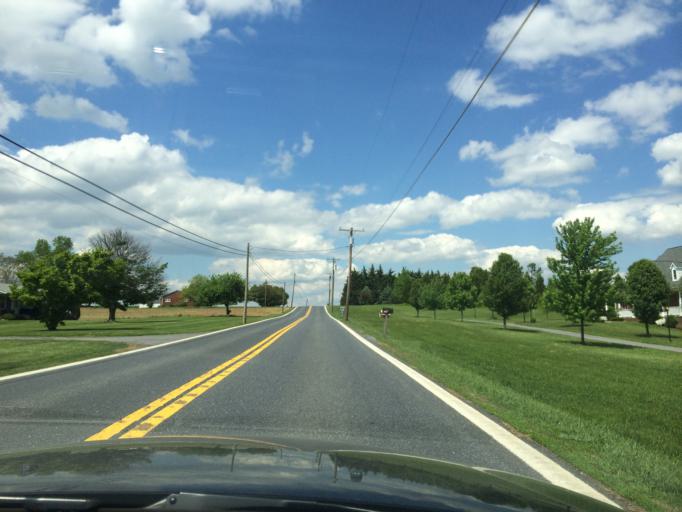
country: US
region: Maryland
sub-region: Frederick County
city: Linganore
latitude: 39.5070
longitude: -77.2401
